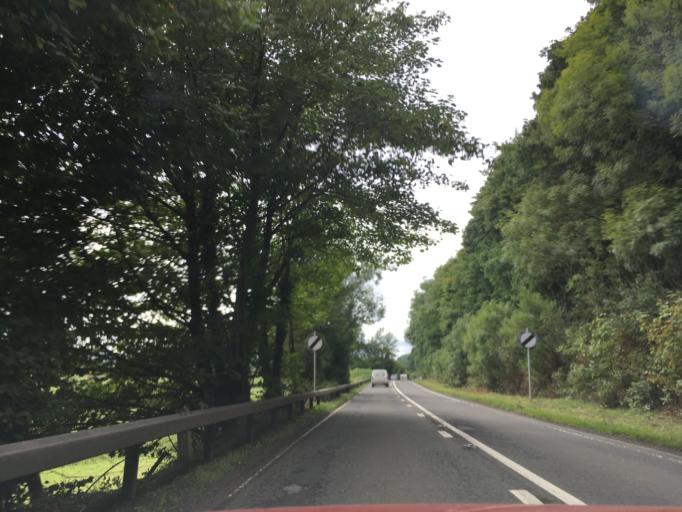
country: GB
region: Wales
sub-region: Carmarthenshire
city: Llanddarog
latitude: 51.8733
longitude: -4.2121
